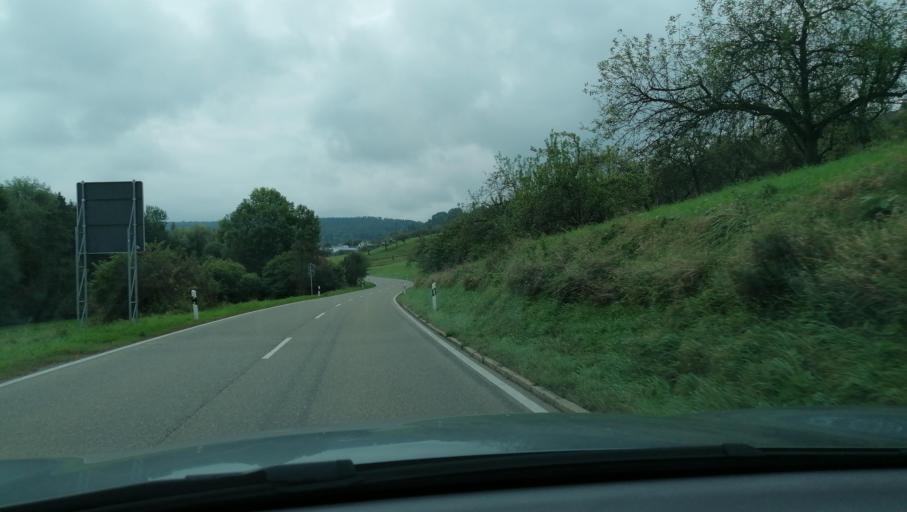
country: DE
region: Baden-Wuerttemberg
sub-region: Regierungsbezirk Stuttgart
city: Winnenden
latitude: 48.8541
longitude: 9.4408
